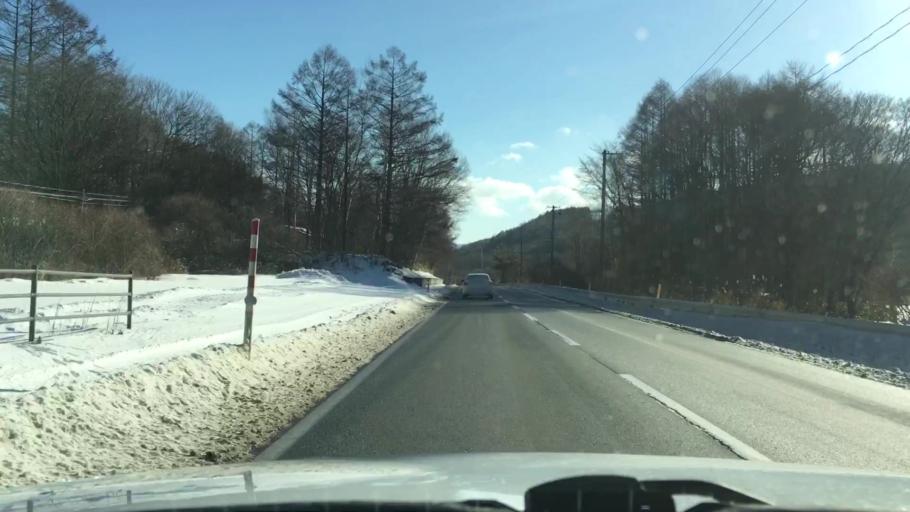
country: JP
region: Iwate
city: Morioka-shi
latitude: 39.6423
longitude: 141.4039
